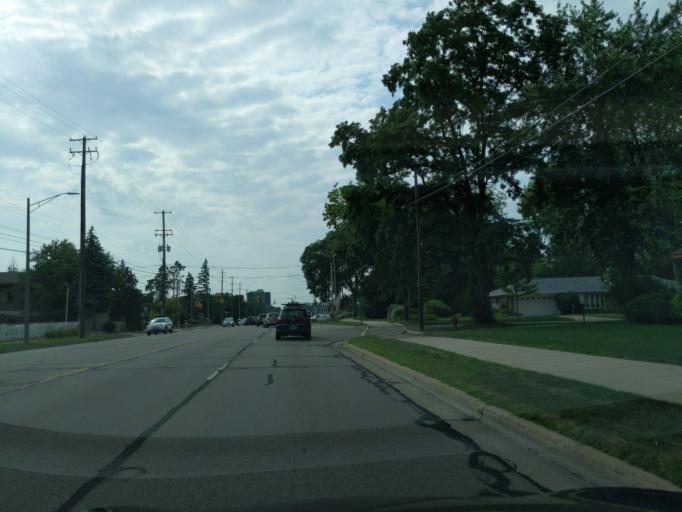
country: US
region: Michigan
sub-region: Ingham County
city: East Lansing
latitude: 42.7290
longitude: -84.4604
